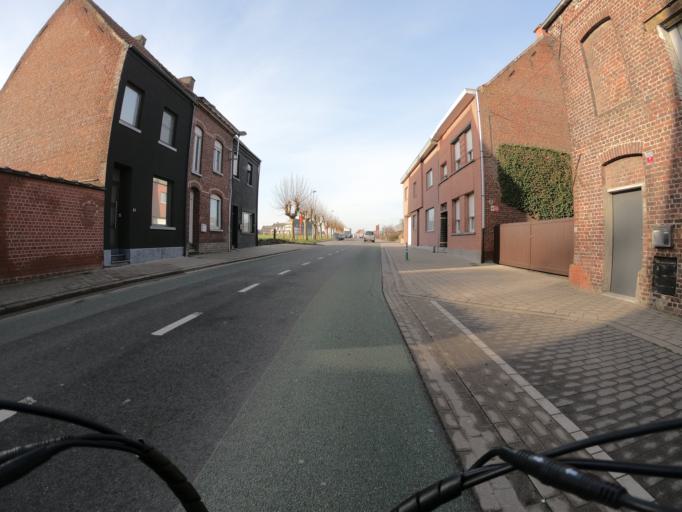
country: BE
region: Flanders
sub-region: Provincie West-Vlaanderen
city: Wevelgem
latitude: 50.7935
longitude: 3.1778
